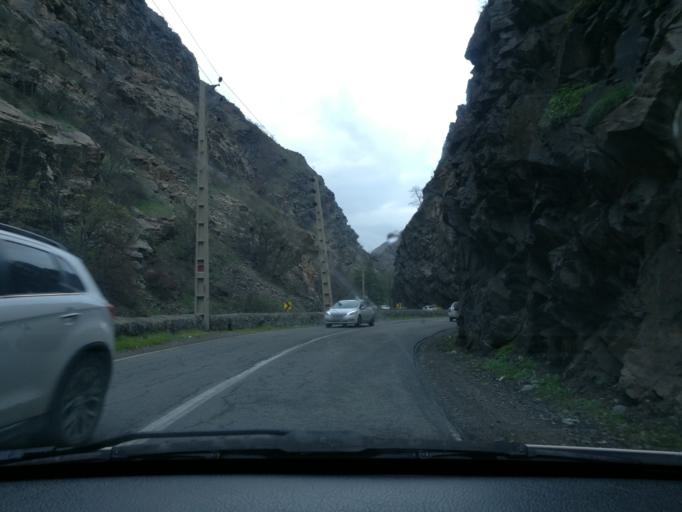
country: IR
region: Mazandaran
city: Chalus
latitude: 36.2957
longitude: 51.2459
